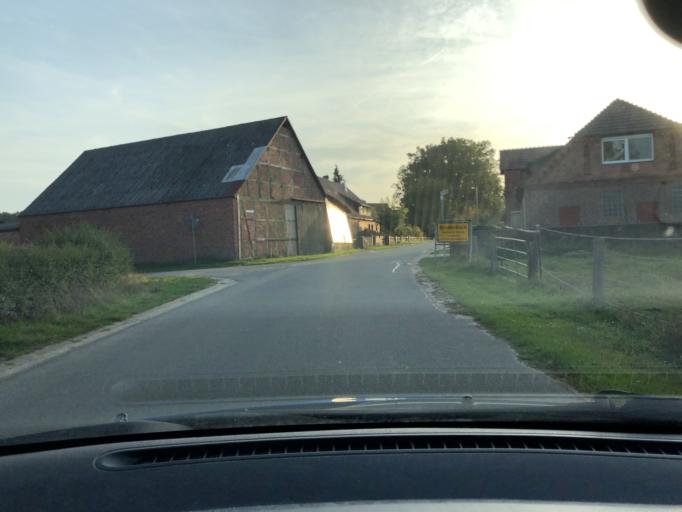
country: DE
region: Lower Saxony
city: Gohrde
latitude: 53.1413
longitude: 10.9584
